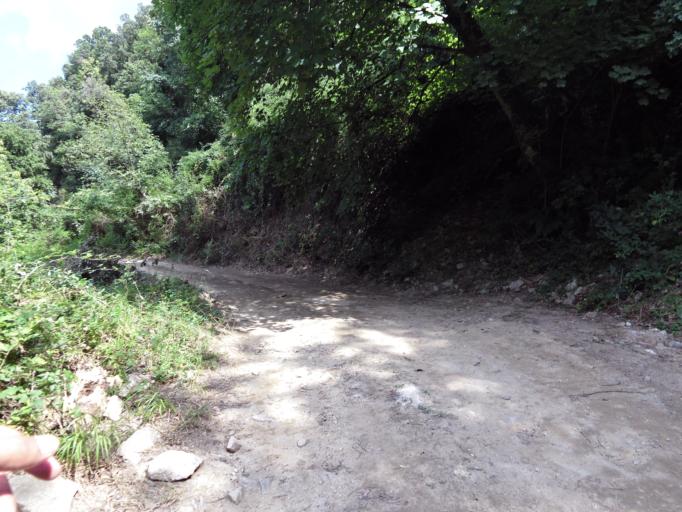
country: IT
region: Calabria
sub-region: Provincia di Reggio Calabria
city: Bivongi
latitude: 38.4956
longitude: 16.4013
